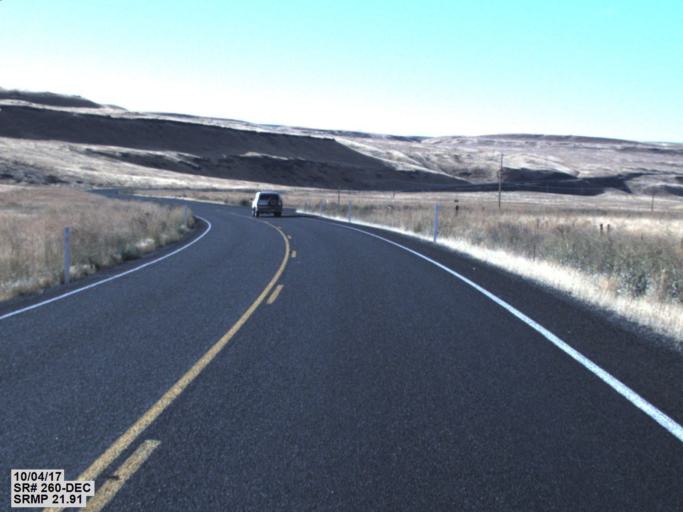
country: US
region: Washington
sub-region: Franklin County
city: Connell
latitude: 46.6476
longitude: -118.6138
